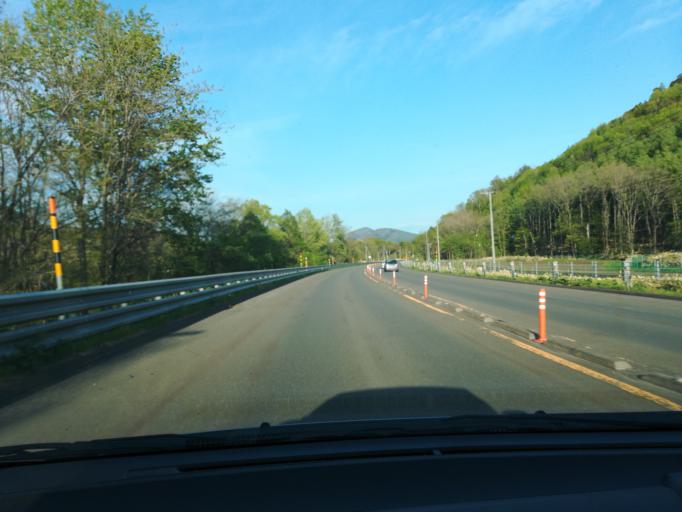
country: JP
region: Hokkaido
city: Shimo-furano
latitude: 43.1384
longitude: 142.6298
